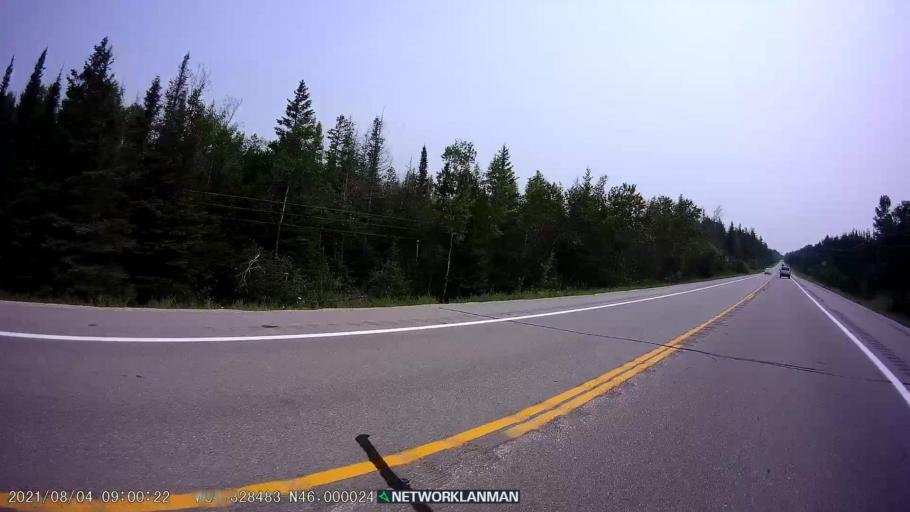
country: US
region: Michigan
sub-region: Cheboygan County
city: Cheboygan
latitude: 46.0000
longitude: -84.3278
